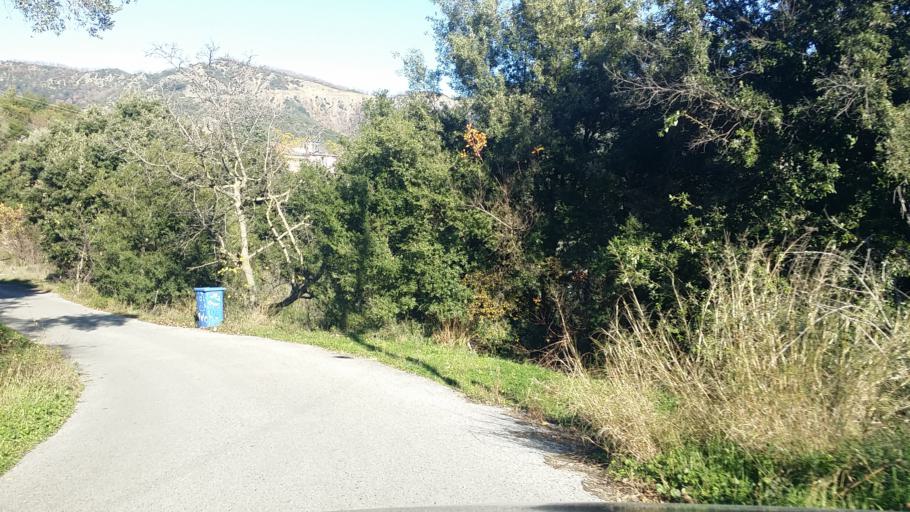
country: GR
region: West Greece
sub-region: Nomos Aitolias kai Akarnanias
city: Krikellos
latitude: 39.0007
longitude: 21.2417
